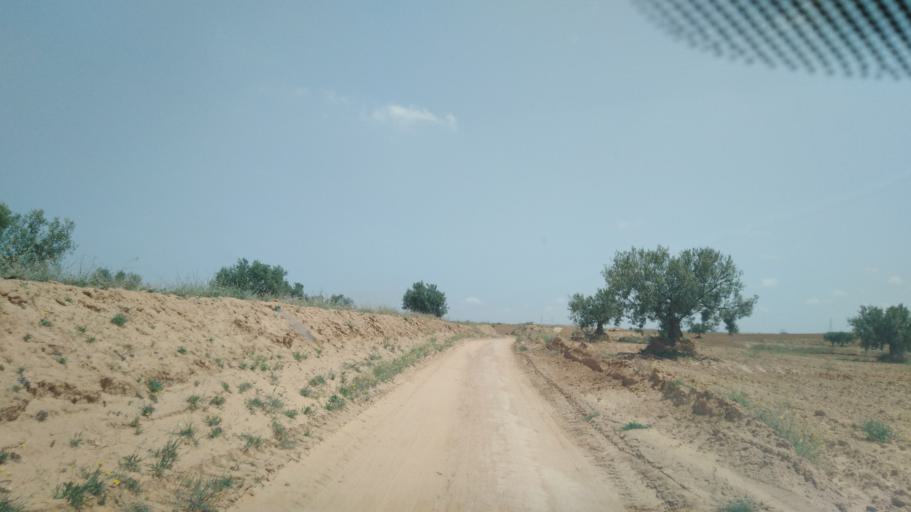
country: TN
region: Safaqis
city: Sfax
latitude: 34.7711
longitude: 10.5751
